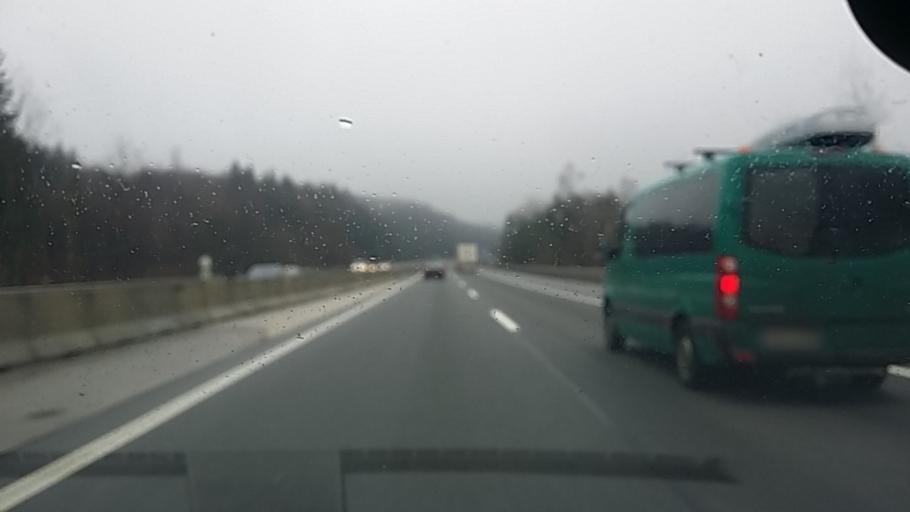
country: AT
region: Lower Austria
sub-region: Politischer Bezirk Baden
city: Klausen-Leopoldsdorf
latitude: 48.1112
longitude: 15.9765
